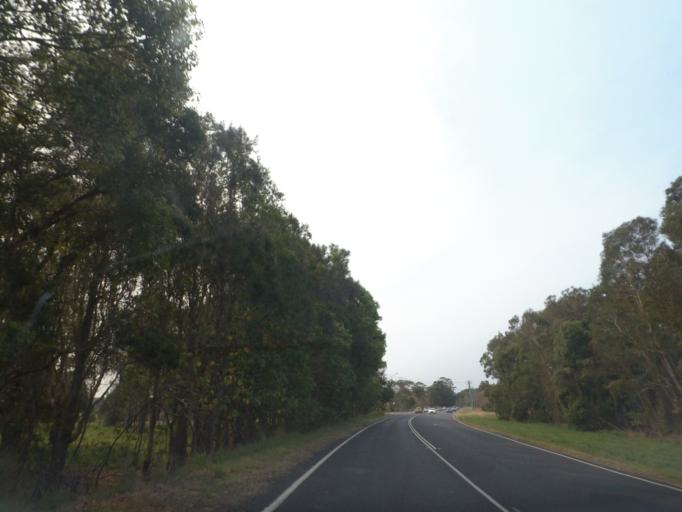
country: AU
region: New South Wales
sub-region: Tweed
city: Kingscliff
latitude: -28.2581
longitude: 153.5600
